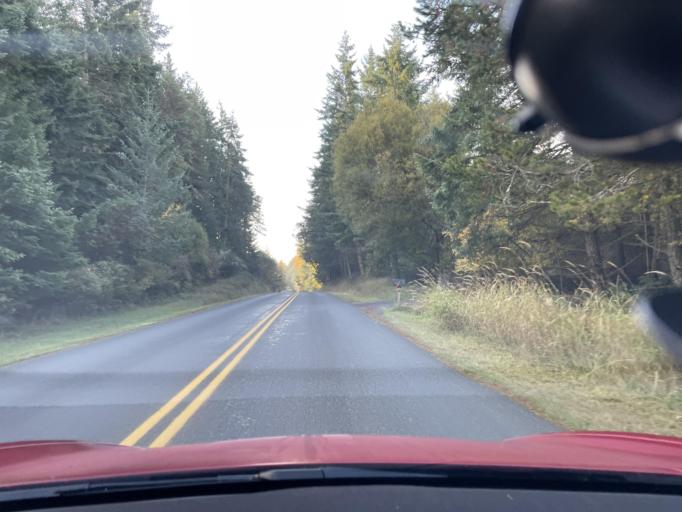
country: US
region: Washington
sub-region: San Juan County
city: Friday Harbor
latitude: 48.5630
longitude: -123.1648
